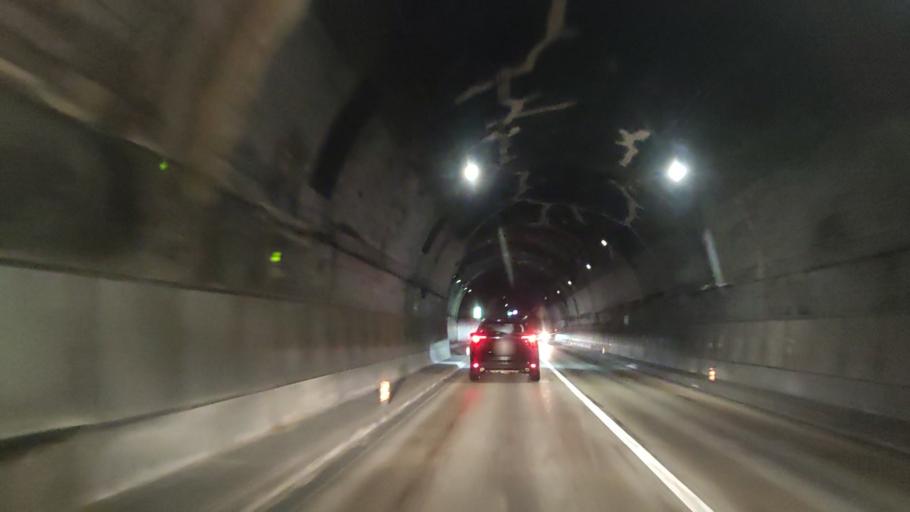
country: JP
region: Tokushima
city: Kamojimacho-jogejima
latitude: 34.1753
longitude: 134.3301
